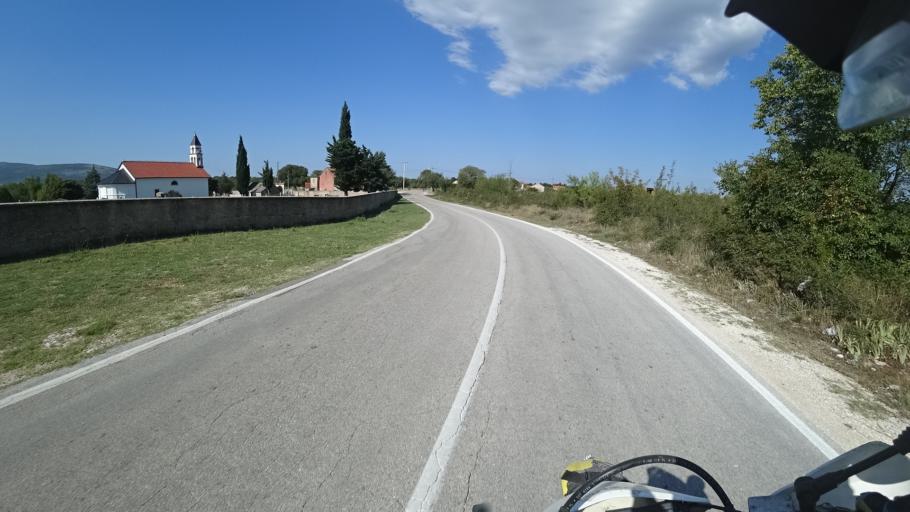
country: HR
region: Sibensko-Kniniska
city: Knin
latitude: 44.0097
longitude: 16.1952
